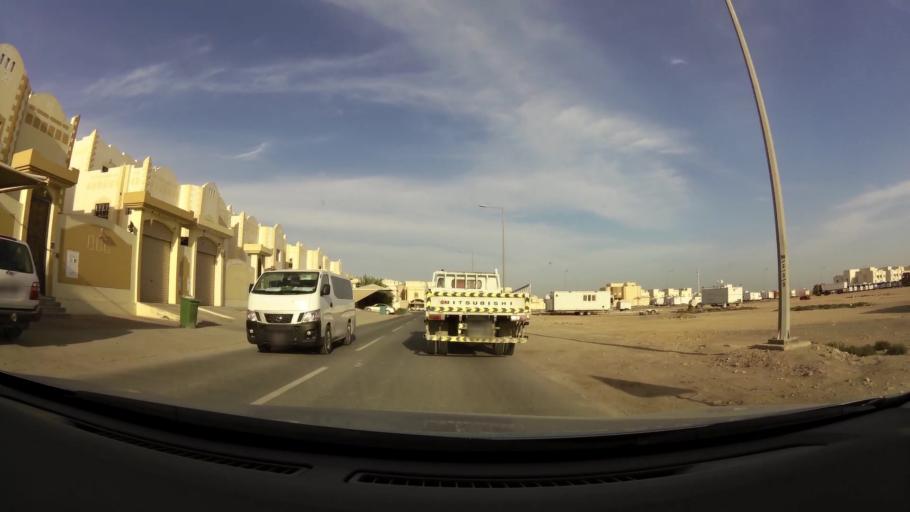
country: QA
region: Al Wakrah
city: Al Wakrah
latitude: 25.1443
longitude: 51.6104
